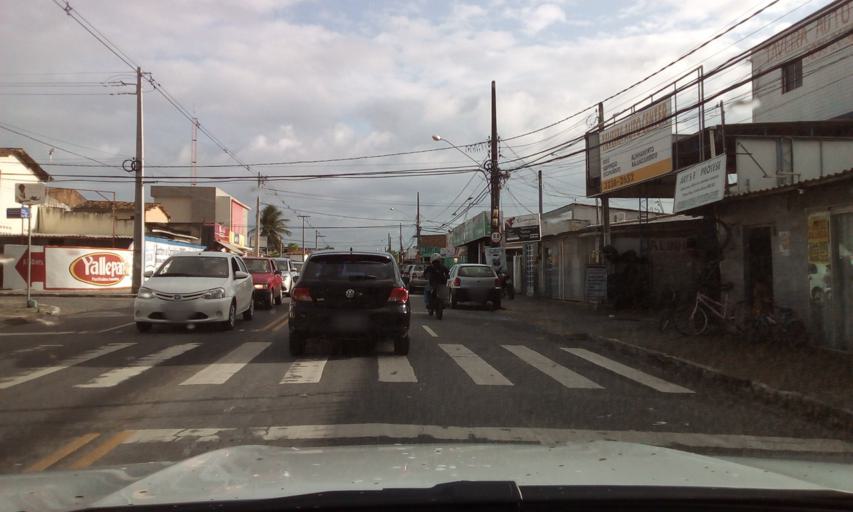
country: BR
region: Paraiba
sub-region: Joao Pessoa
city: Joao Pessoa
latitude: -7.1664
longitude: -34.8422
